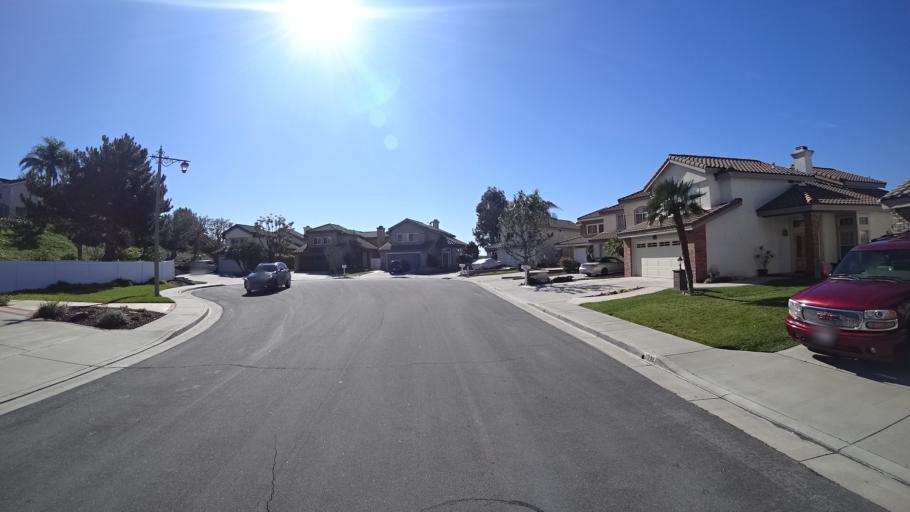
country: US
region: California
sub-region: Orange County
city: Villa Park
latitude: 33.8490
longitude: -117.7430
